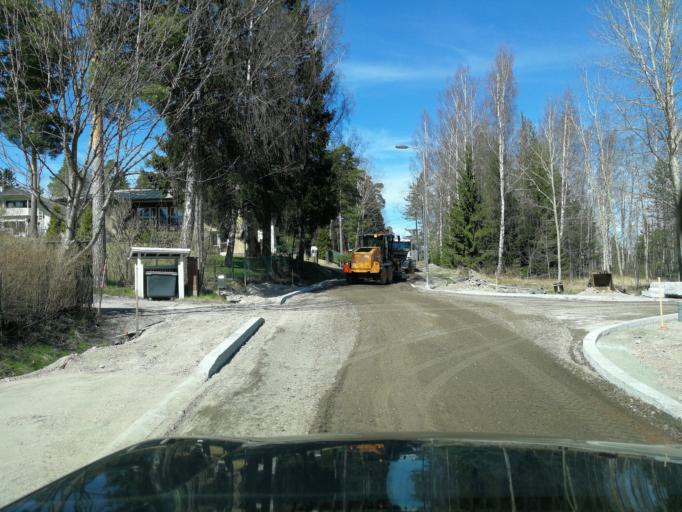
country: FI
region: Uusimaa
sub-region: Helsinki
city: Kauniainen
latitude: 60.1657
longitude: 24.6980
